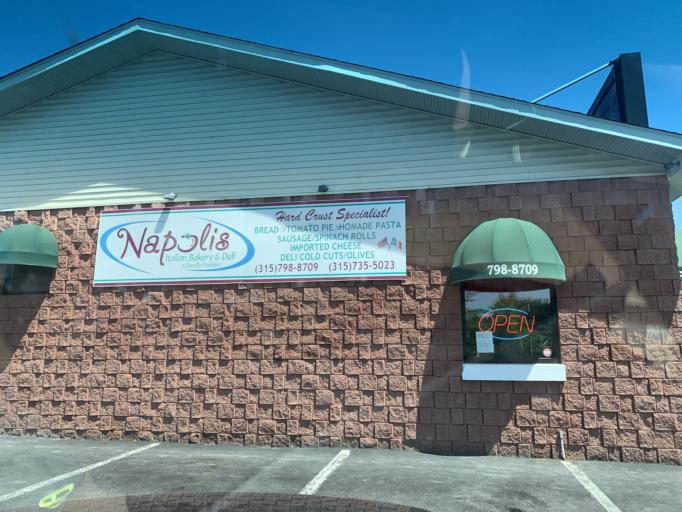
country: US
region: New York
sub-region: Oneida County
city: Utica
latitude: 43.0920
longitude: -75.1968
